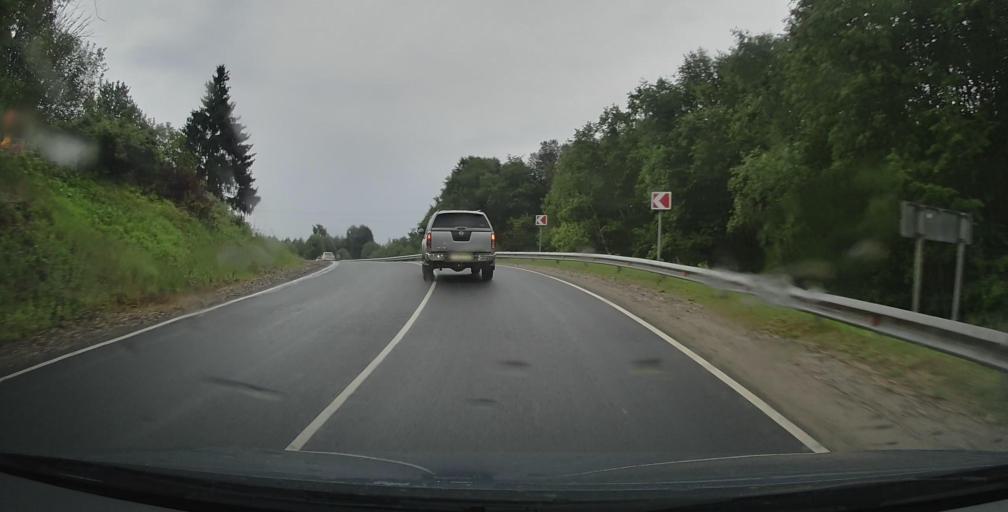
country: RU
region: Jaroslavl
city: Uglich
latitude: 57.5565
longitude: 38.2752
